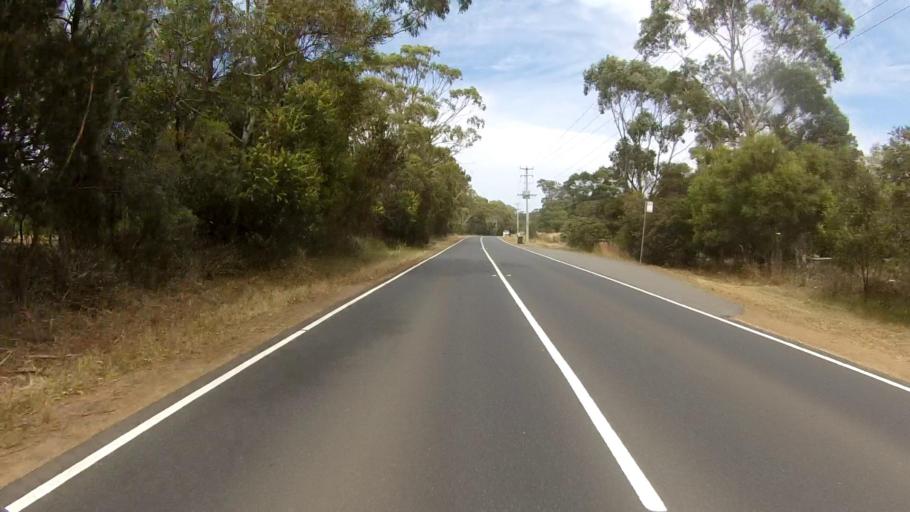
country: AU
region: Tasmania
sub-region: Clarence
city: Acton Park
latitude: -42.8751
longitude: 147.4829
